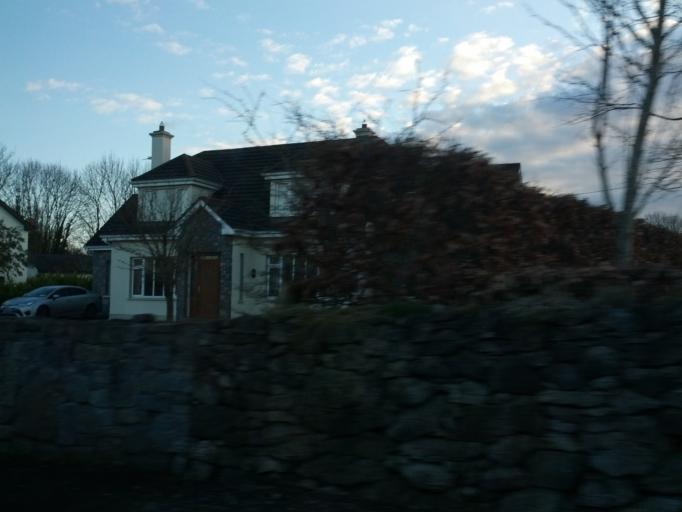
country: IE
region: Connaught
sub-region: County Galway
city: Athenry
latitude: 53.3384
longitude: -8.7094
